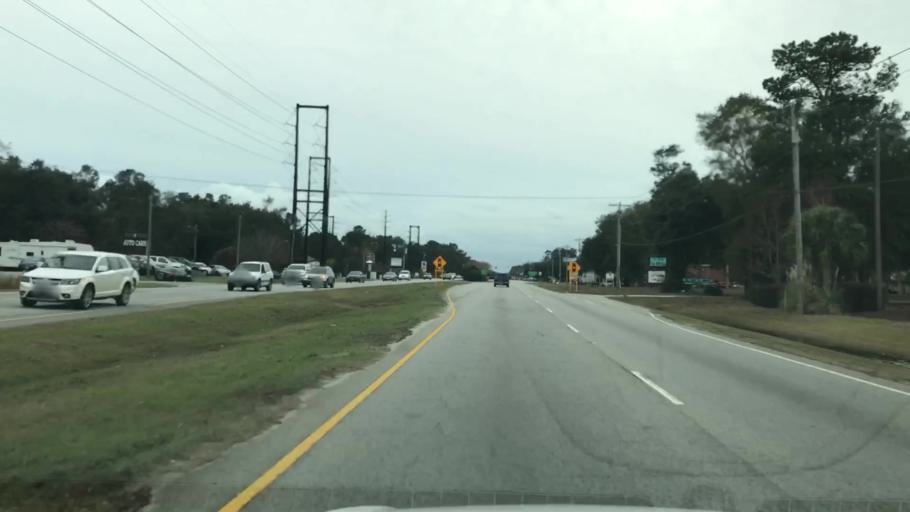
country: US
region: South Carolina
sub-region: Georgetown County
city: Murrells Inlet
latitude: 33.5530
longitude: -79.0462
